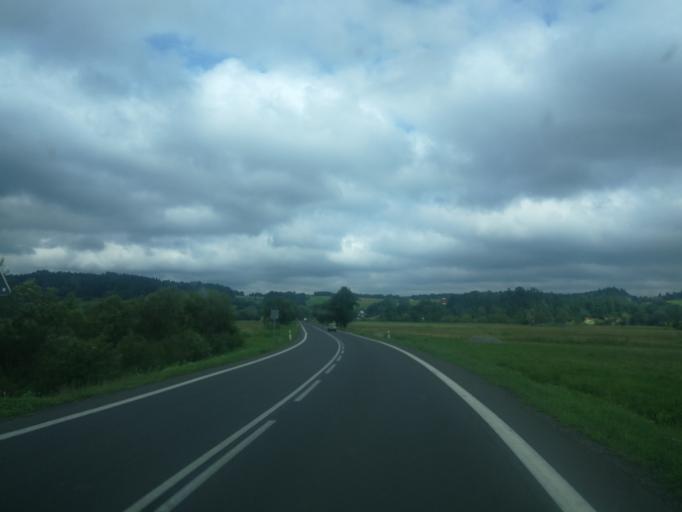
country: PL
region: Subcarpathian Voivodeship
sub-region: Powiat leski
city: Lesko
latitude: 49.4918
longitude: 22.3191
